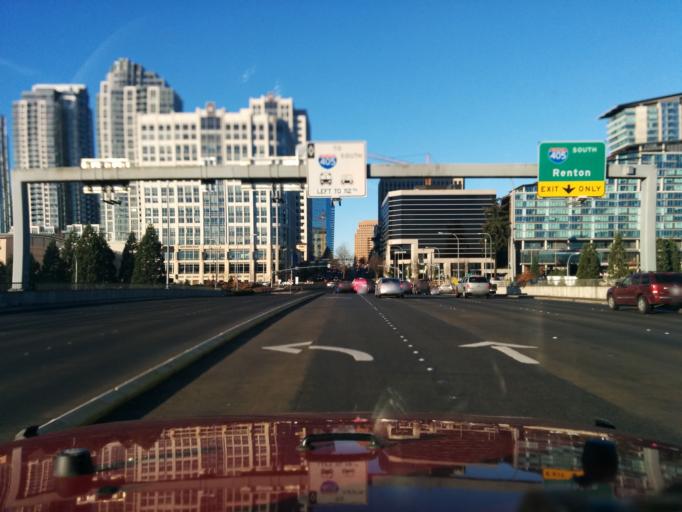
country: US
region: Washington
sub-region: King County
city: Bellevue
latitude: 47.6173
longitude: -122.1882
